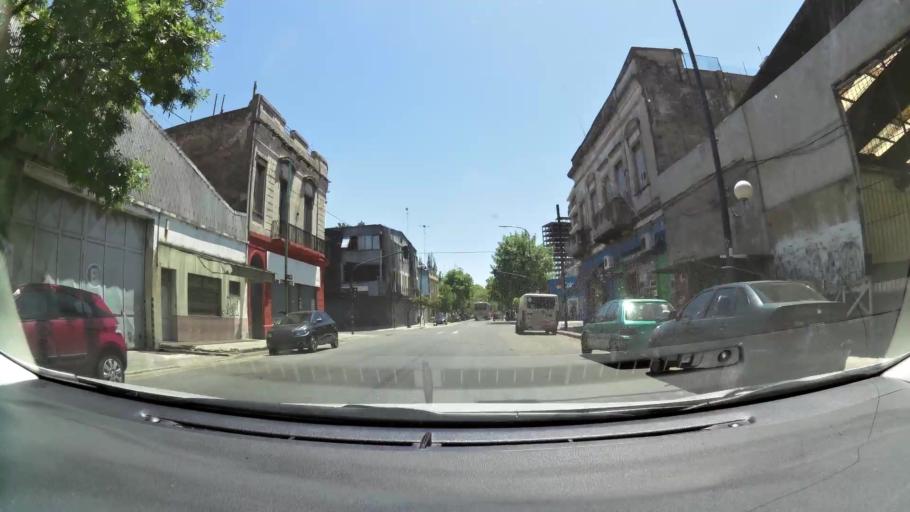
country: AR
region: Buenos Aires
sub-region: Partido de Avellaneda
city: Avellaneda
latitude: -34.6452
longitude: -58.3788
